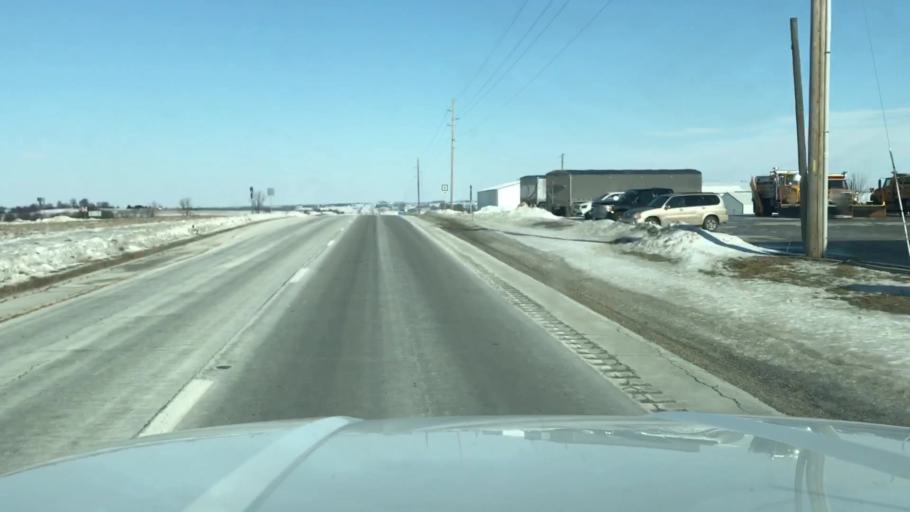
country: US
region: Missouri
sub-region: Andrew County
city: Savannah
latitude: 40.1132
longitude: -94.8697
